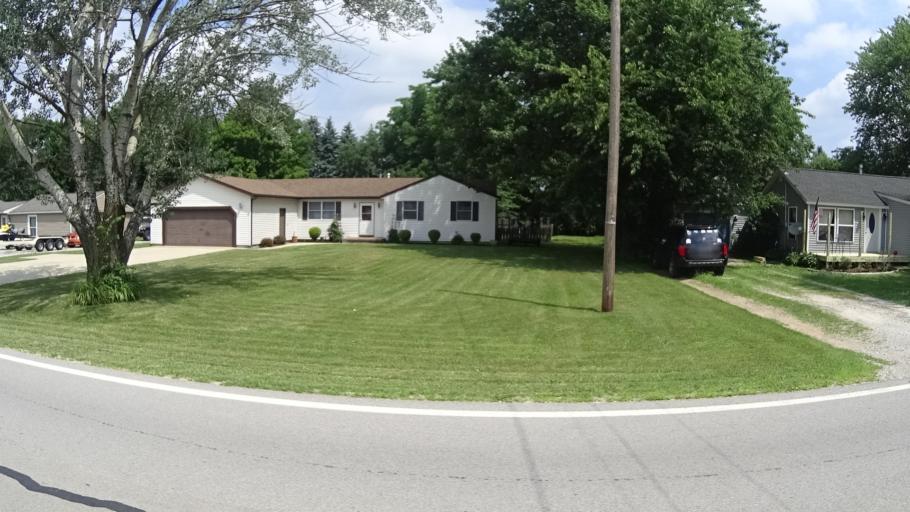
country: US
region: Ohio
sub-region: Lorain County
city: Vermilion
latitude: 41.3695
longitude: -82.3593
